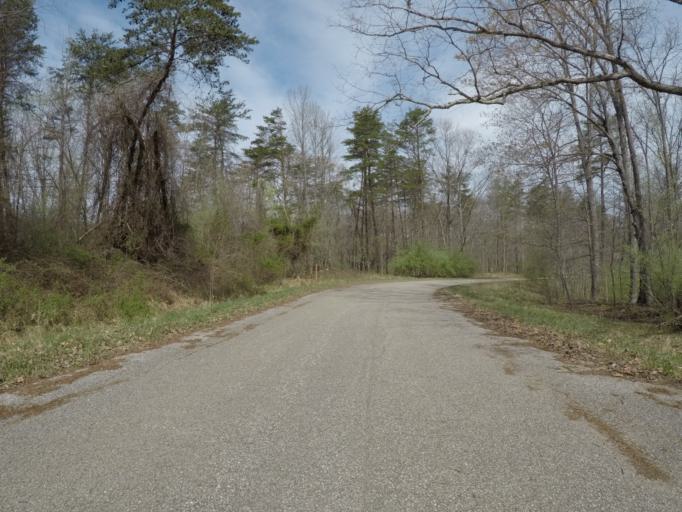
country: US
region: West Virginia
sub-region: Cabell County
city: Pea Ridge
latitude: 38.3232
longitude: -82.3506
